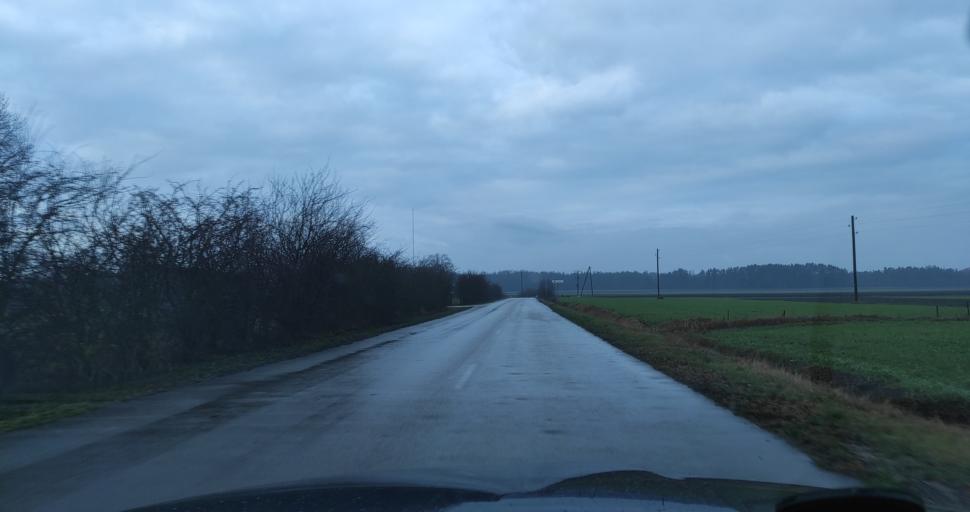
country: LV
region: Ventspils
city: Ventspils
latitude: 57.2384
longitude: 21.4380
